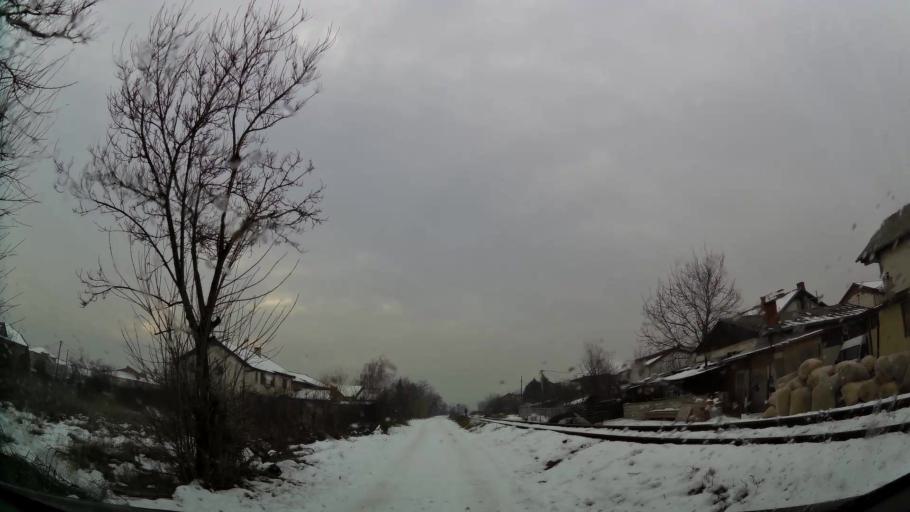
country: MK
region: Saraj
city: Saraj
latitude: 42.0374
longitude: 21.3515
